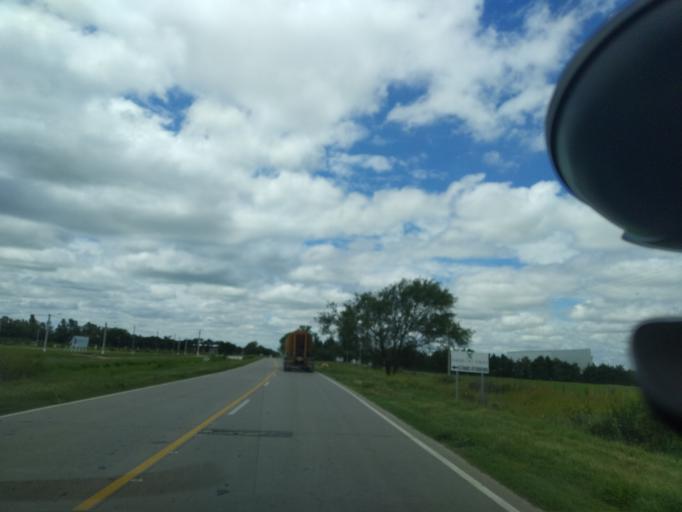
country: AR
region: Cordoba
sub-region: Departamento de Rio Segundo
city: Rio Segundo
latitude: -31.6381
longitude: -63.8911
